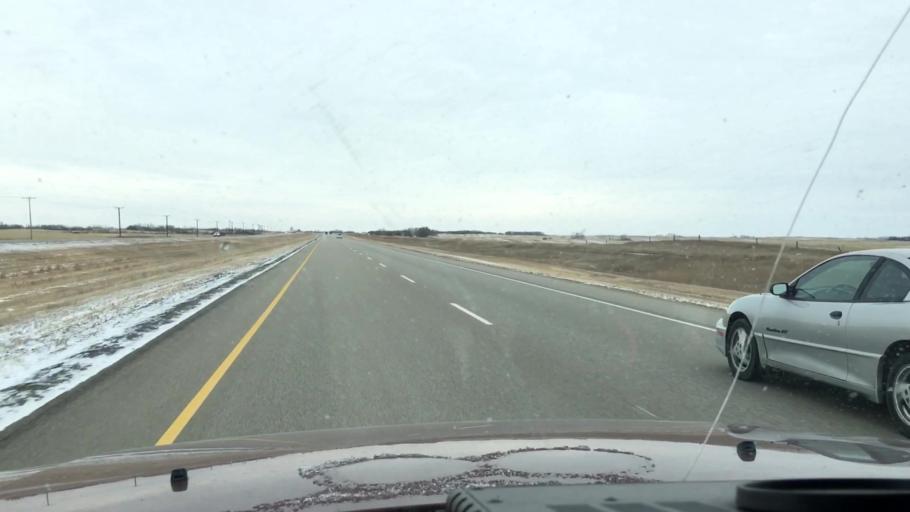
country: CA
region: Saskatchewan
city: Watrous
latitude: 51.4018
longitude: -106.1778
